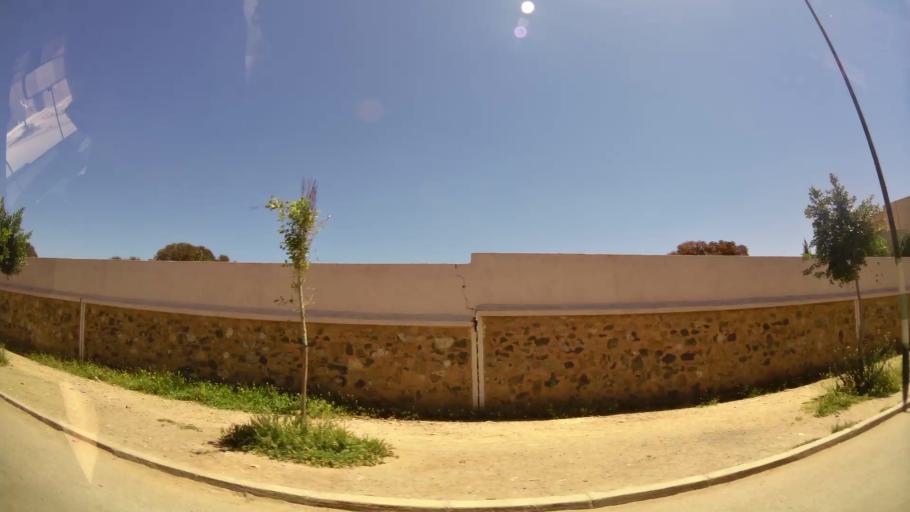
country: MA
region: Oriental
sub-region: Oujda-Angad
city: Oujda
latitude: 34.6691
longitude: -1.8824
